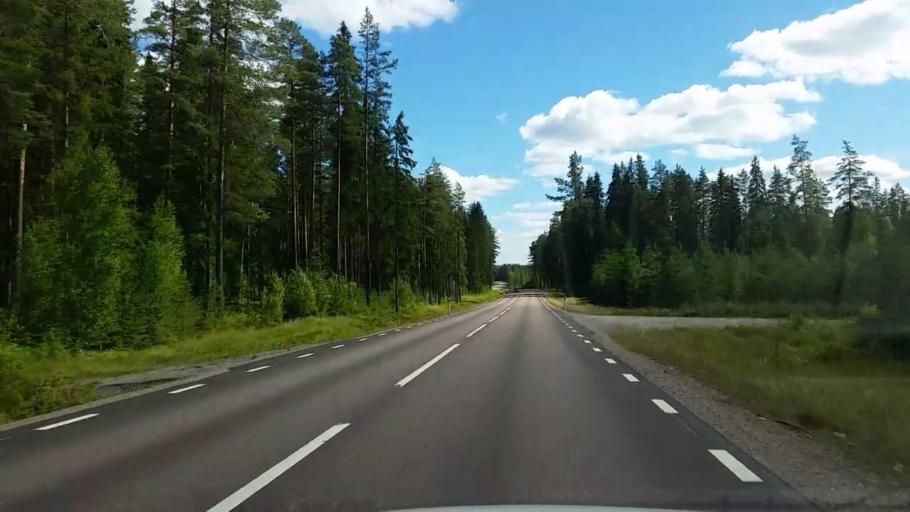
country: SE
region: Dalarna
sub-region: Faluns Kommun
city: Svardsjo
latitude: 60.7599
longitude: 15.7547
